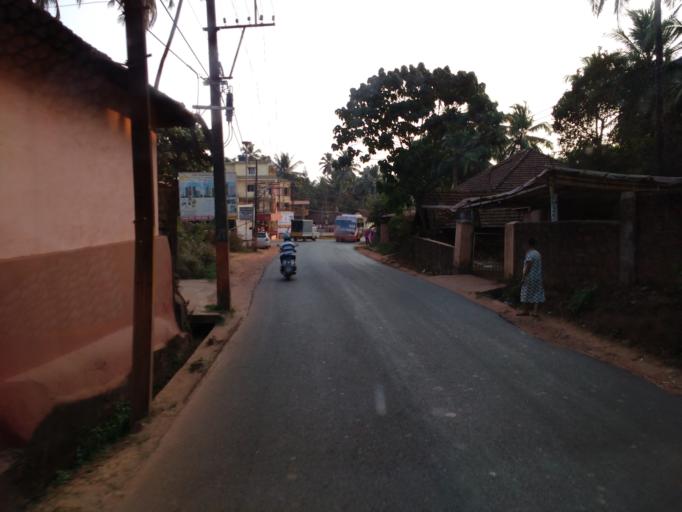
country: IN
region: Karnataka
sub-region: Dakshina Kannada
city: Mangalore
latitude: 12.8890
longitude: 74.8876
